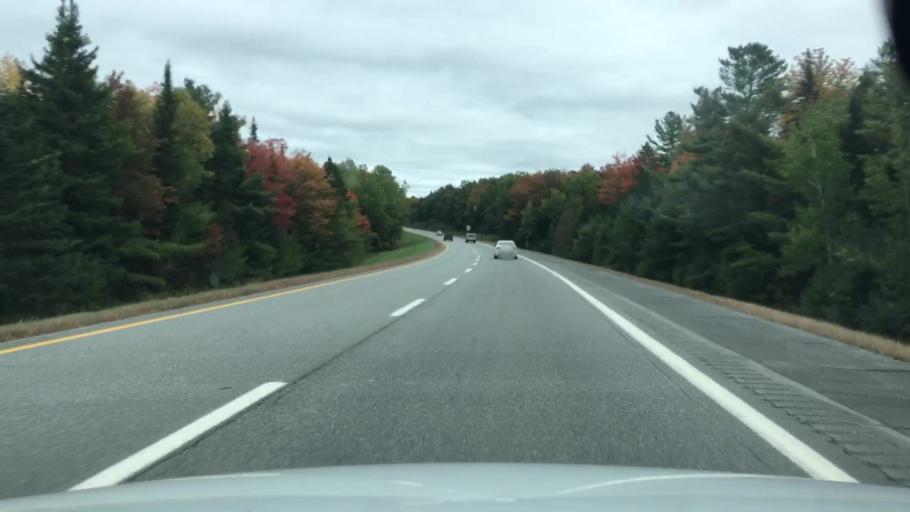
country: US
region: Maine
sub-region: Penobscot County
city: Plymouth
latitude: 44.7918
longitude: -69.2027
